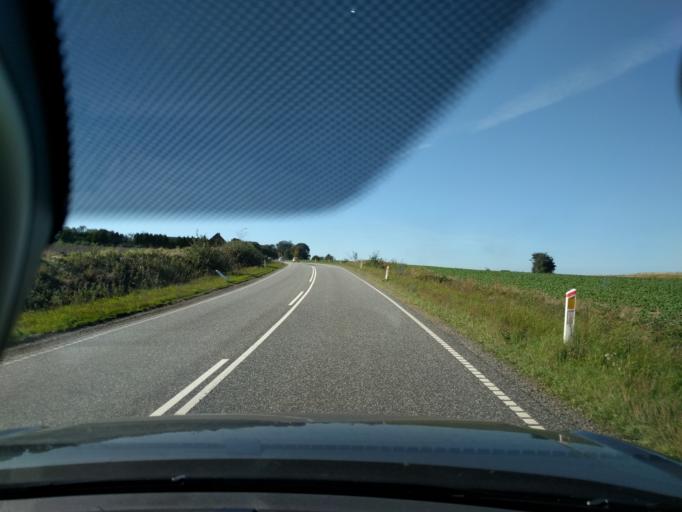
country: DK
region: North Denmark
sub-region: Mariagerfjord Kommune
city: Hobro
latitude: 56.6728
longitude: 9.6971
